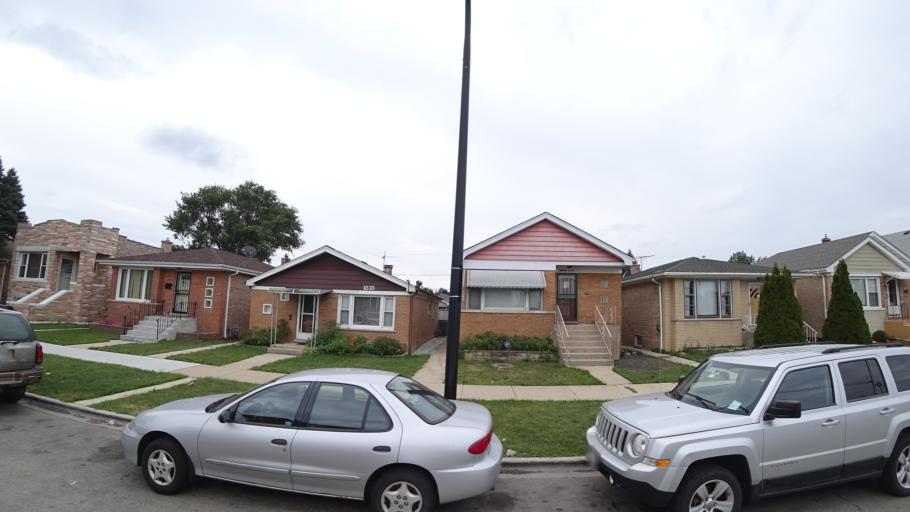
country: US
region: Illinois
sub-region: Cook County
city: Cicero
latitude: 41.8557
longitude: -87.7616
